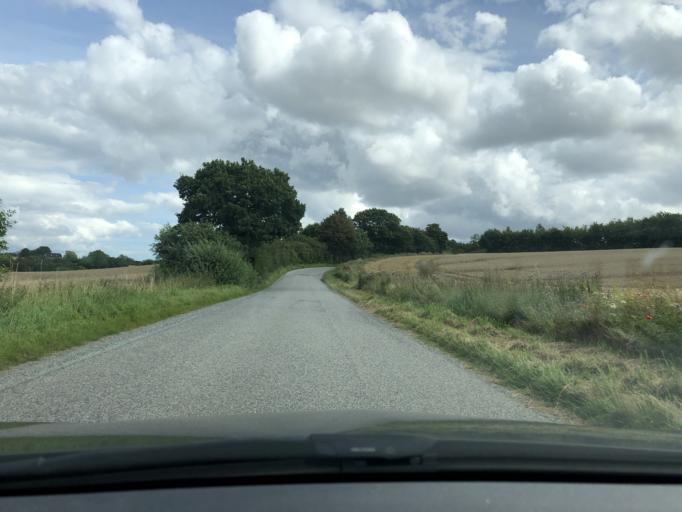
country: DK
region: South Denmark
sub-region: Vejle Kommune
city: Jelling
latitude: 55.6953
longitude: 9.4564
